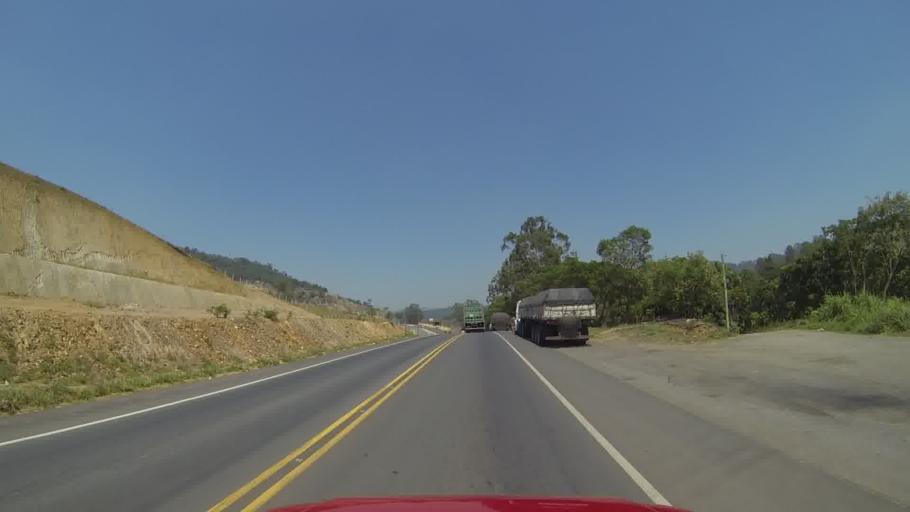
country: BR
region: Minas Gerais
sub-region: Mateus Leme
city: Mateus Leme
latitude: -20.0137
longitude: -44.4844
